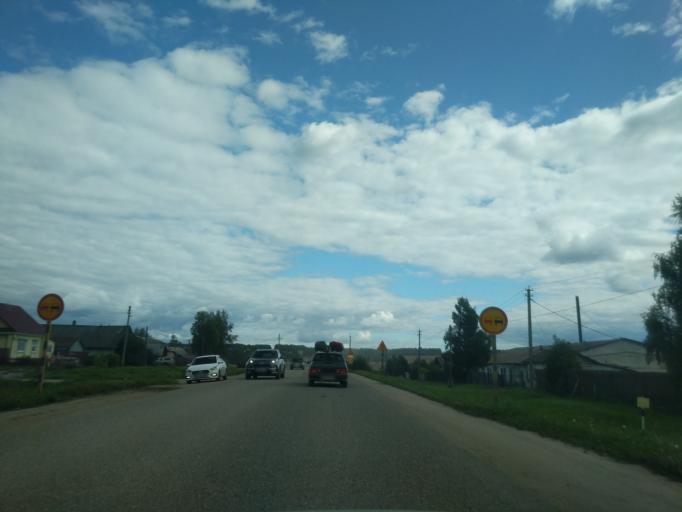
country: RU
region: Kostroma
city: Sudislavl'
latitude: 57.8781
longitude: 41.7260
